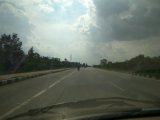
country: IN
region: Karnataka
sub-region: Kolar
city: Malur
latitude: 13.1304
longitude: 77.9602
